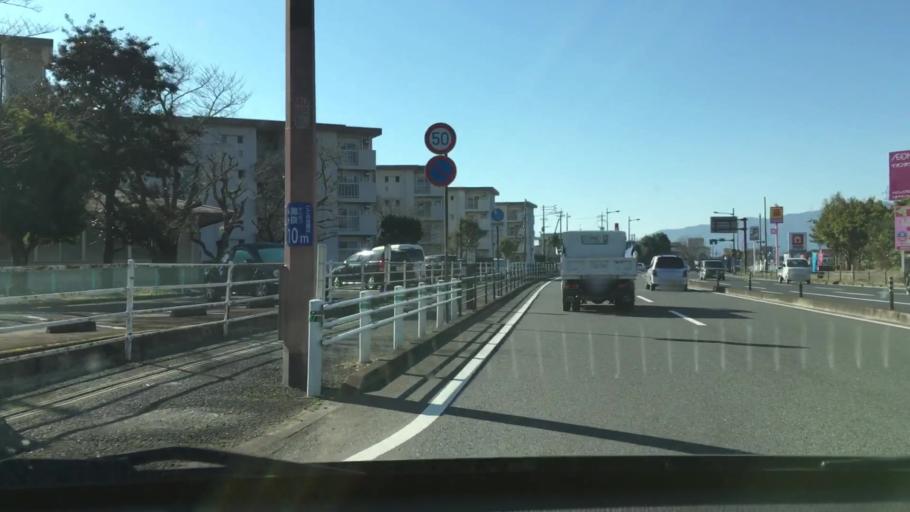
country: JP
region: Kagoshima
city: Kajiki
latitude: 31.7404
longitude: 130.6521
